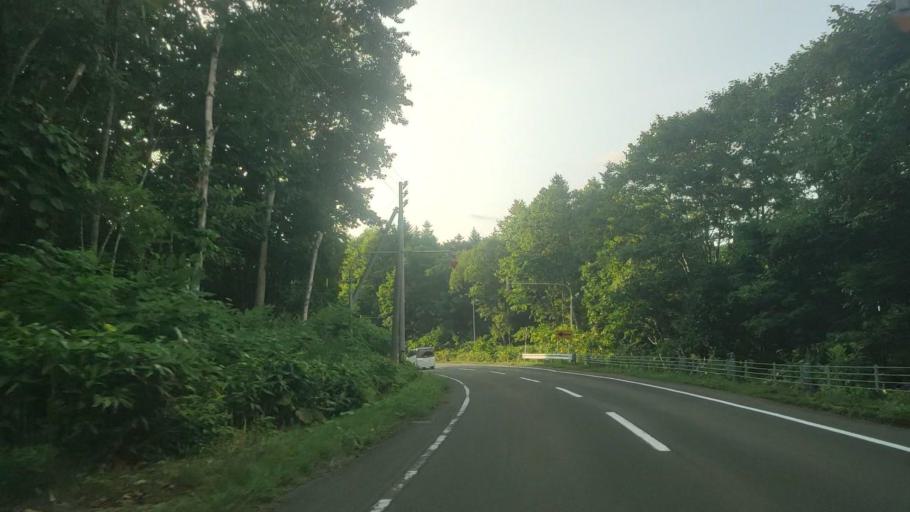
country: JP
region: Hokkaido
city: Bibai
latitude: 43.1773
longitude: 142.0695
